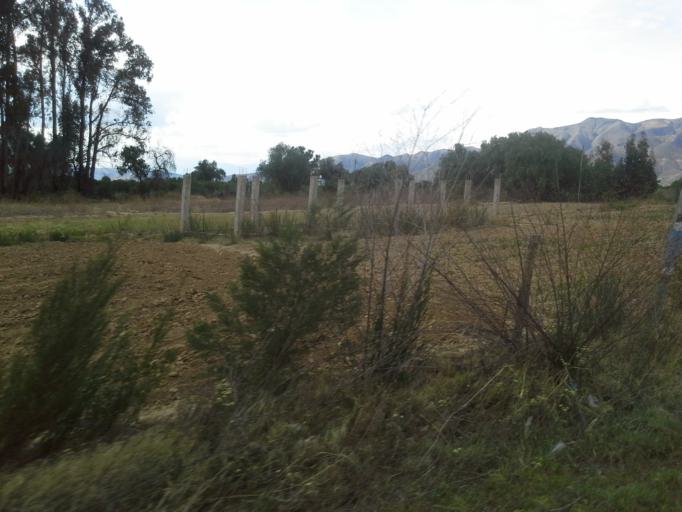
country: BO
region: Cochabamba
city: Tarata
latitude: -17.5727
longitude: -66.0140
